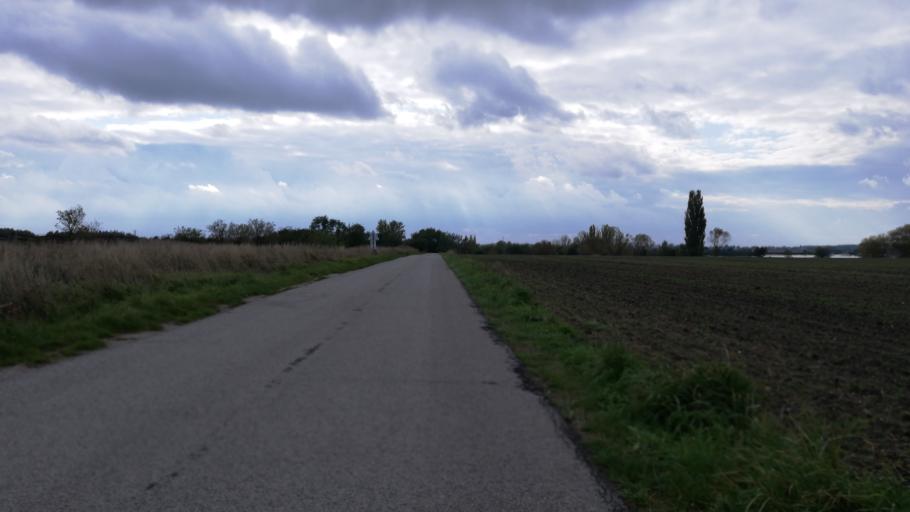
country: SK
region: Trnavsky
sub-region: Okres Skalica
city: Skalica
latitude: 48.8414
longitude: 17.2085
